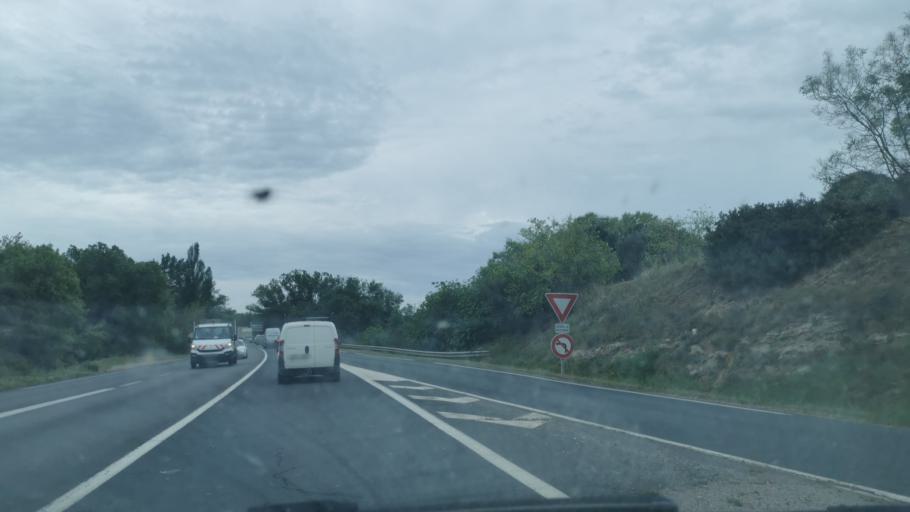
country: FR
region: Languedoc-Roussillon
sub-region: Departement de l'Herault
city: Balaruc-le-Vieux
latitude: 43.4715
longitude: 3.6878
